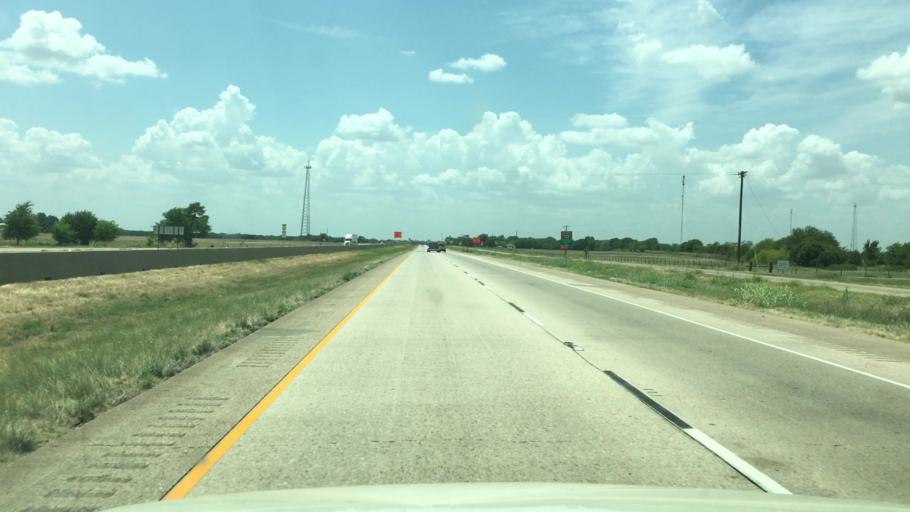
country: US
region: Texas
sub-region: Hunt County
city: Commerce
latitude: 33.1316
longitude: -95.7904
